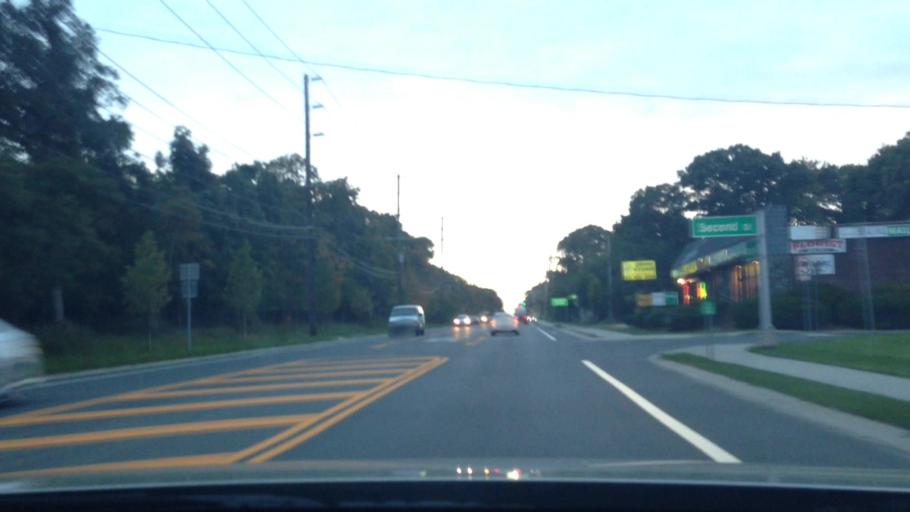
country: US
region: New York
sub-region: Suffolk County
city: Coram
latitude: 40.8624
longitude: -72.9989
